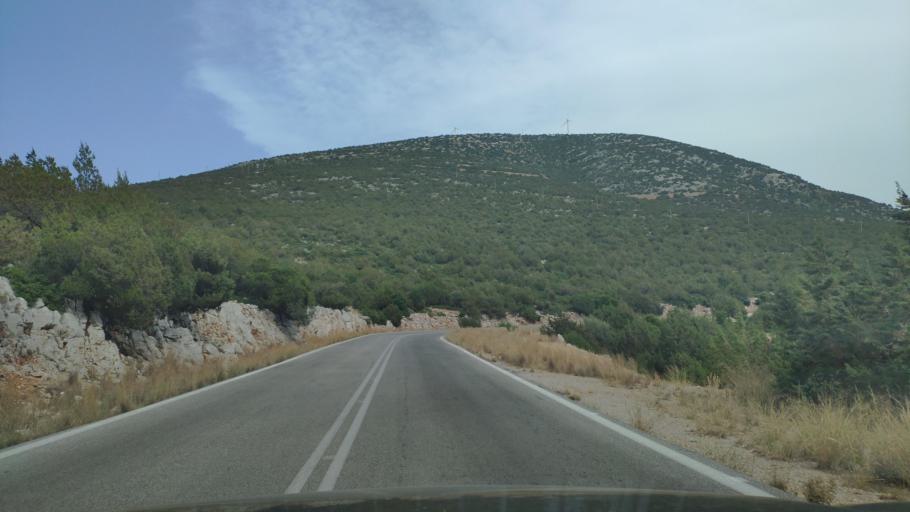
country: GR
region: Peloponnese
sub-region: Nomos Argolidos
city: Didyma
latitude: 37.5040
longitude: 23.1915
